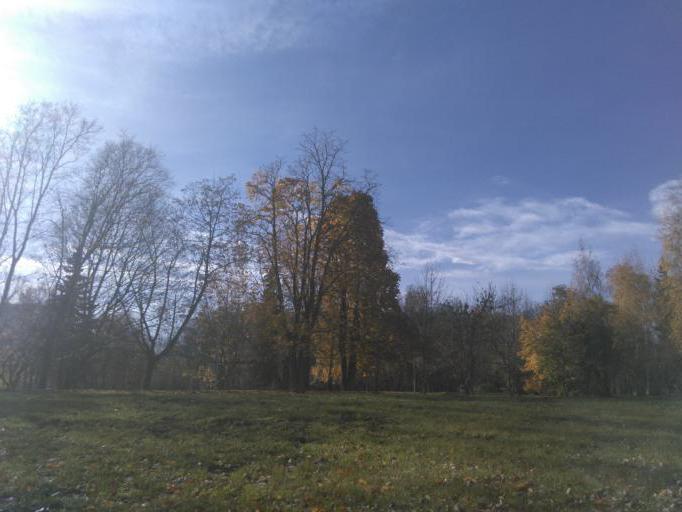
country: RU
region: Moskovskaya
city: Leninskiye Gory
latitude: 55.7012
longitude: 37.5661
